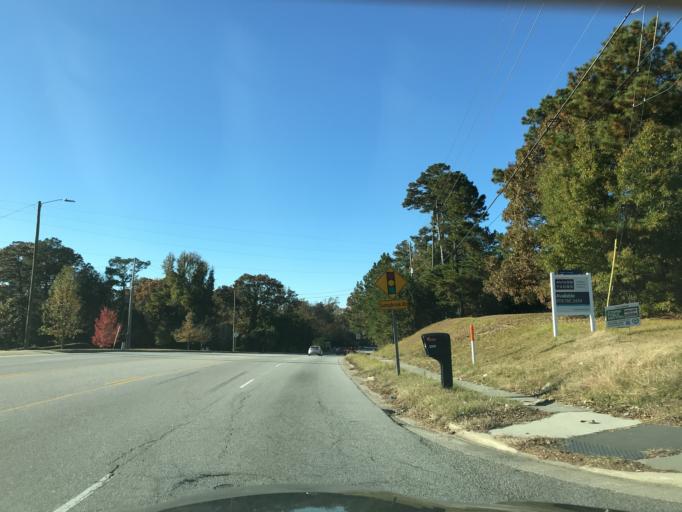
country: US
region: North Carolina
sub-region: Wake County
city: Raleigh
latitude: 35.7692
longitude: -78.5809
